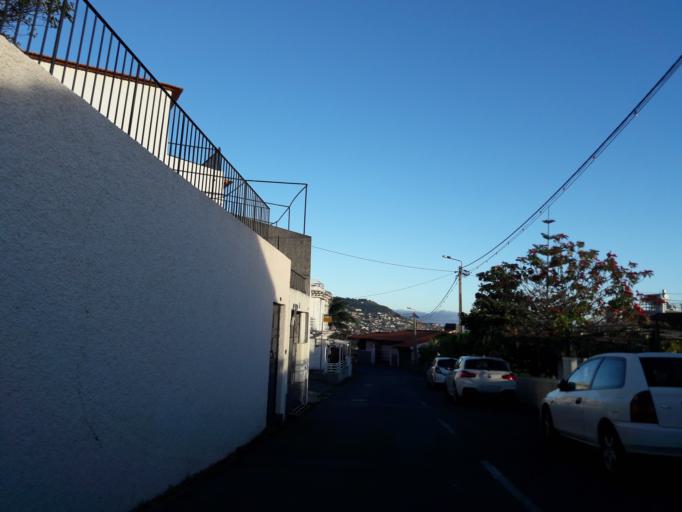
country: PT
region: Madeira
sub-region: Funchal
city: Nossa Senhora do Monte
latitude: 32.6662
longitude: -16.9138
